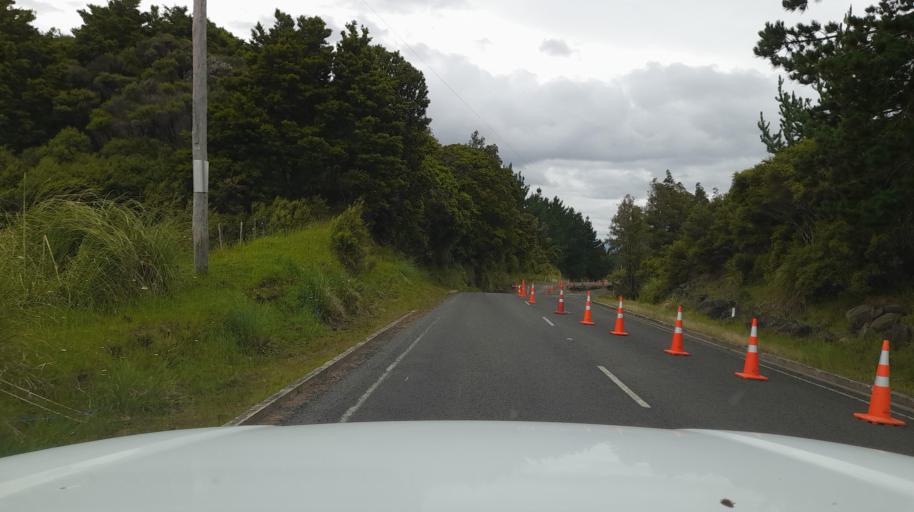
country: NZ
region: Northland
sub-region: Far North District
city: Kaitaia
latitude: -35.3656
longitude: 173.4088
